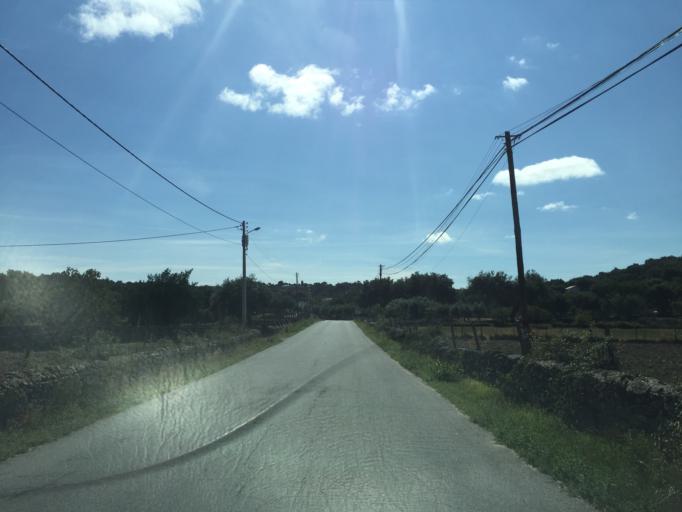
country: PT
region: Portalegre
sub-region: Marvao
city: Marvao
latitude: 39.4276
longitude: -7.3561
